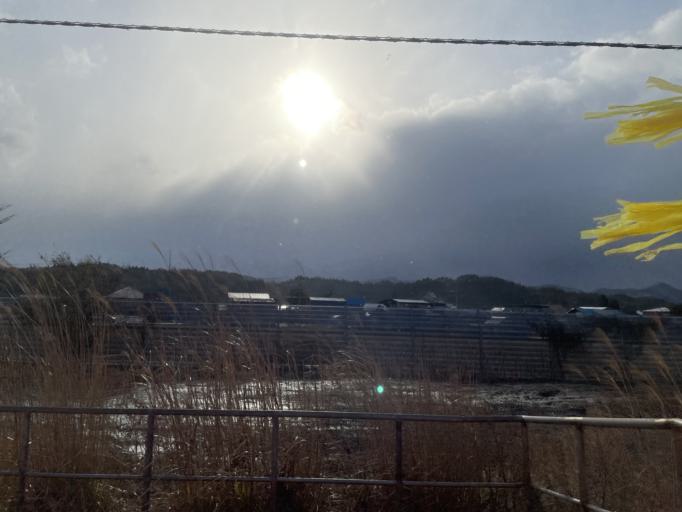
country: JP
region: Aomori
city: Aomori Shi
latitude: 41.0516
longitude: 140.5967
